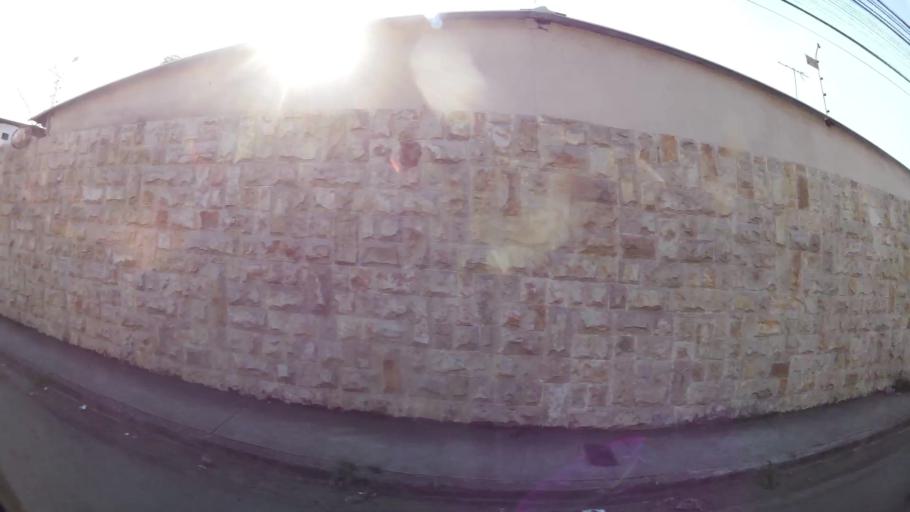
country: EC
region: Guayas
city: Guayaquil
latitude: -2.1564
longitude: -79.9112
